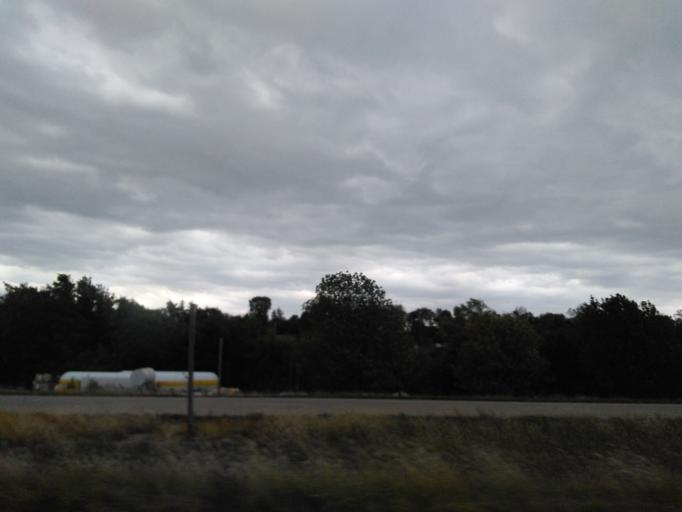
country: US
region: Illinois
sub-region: Monroe County
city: Columbia
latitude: 38.4767
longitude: -90.2244
